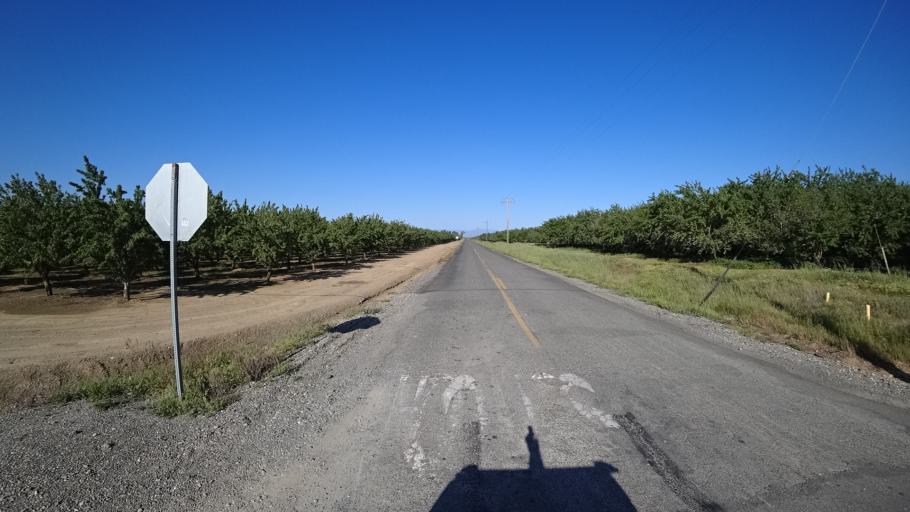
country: US
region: California
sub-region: Glenn County
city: Hamilton City
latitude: 39.6959
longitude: -122.1033
